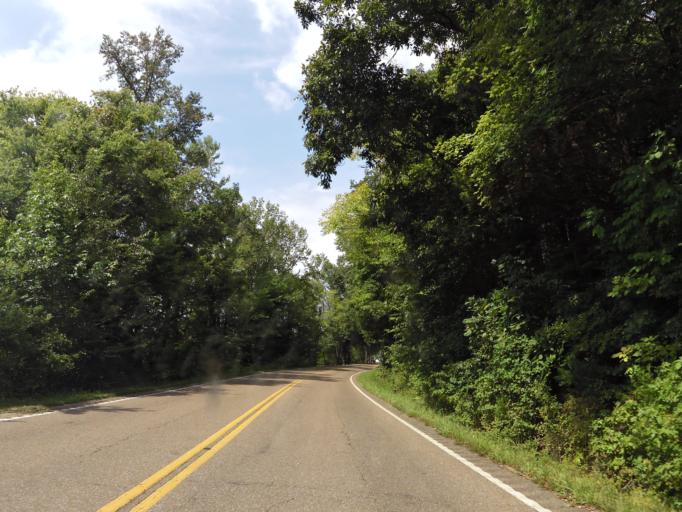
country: US
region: Tennessee
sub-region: Perry County
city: Linden
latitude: 35.6218
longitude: -87.9314
